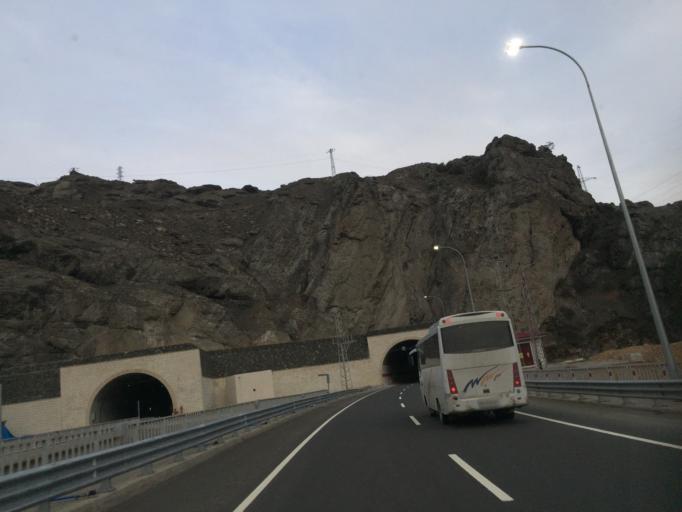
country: TR
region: Gumushane
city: Gumushkhane
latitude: 40.5006
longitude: 39.4362
